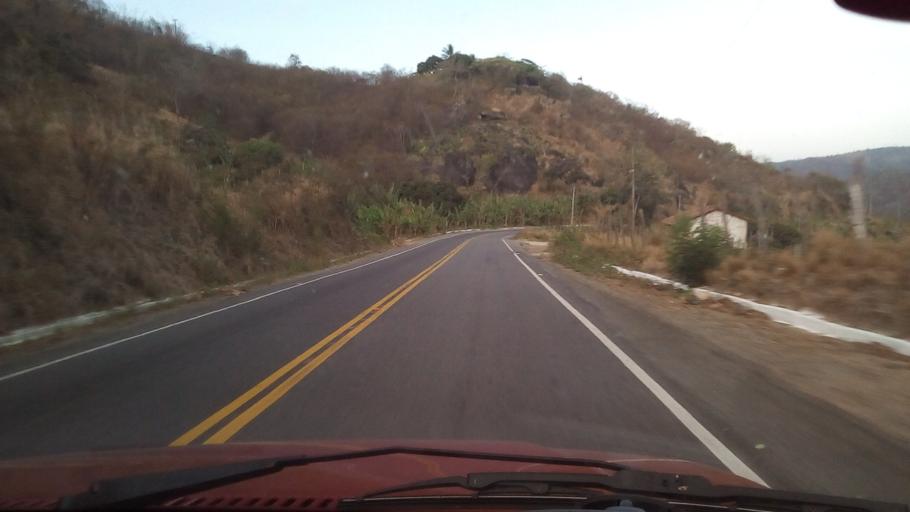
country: BR
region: Paraiba
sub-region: Bananeiras
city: Solanea
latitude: -6.7387
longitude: -35.5613
